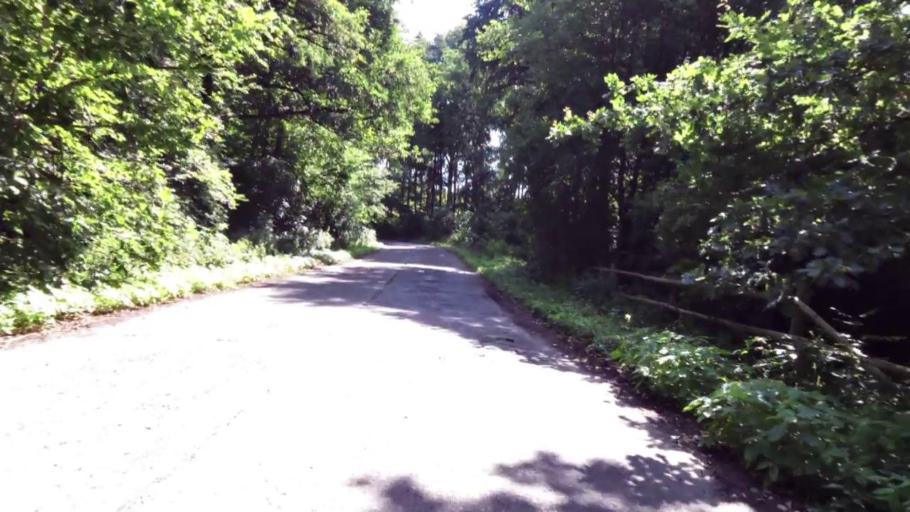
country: PL
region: West Pomeranian Voivodeship
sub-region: Powiat stargardzki
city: Dobrzany
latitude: 53.3886
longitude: 15.4935
